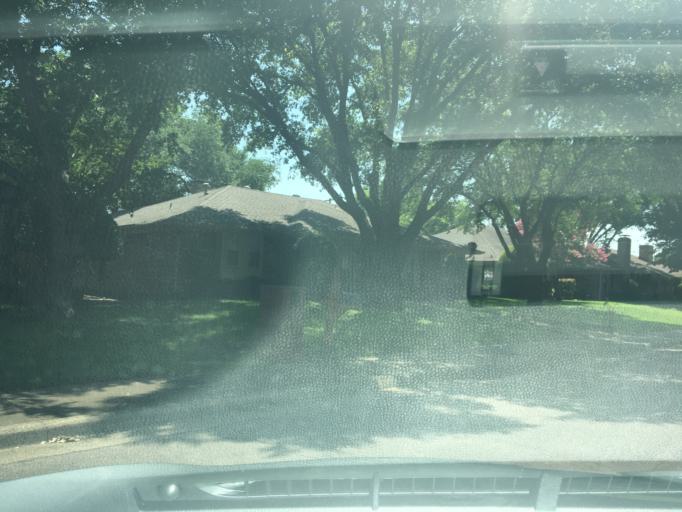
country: US
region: Texas
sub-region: Dallas County
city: Richardson
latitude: 32.9301
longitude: -96.7072
